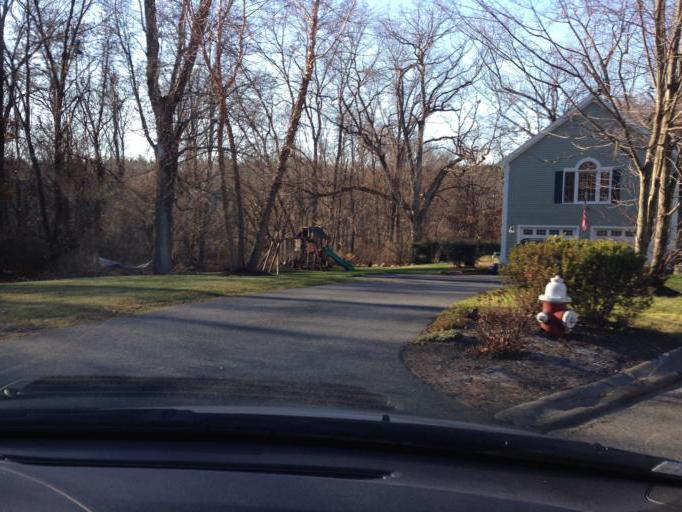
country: US
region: Massachusetts
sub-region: Middlesex County
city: Bedford
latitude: 42.5156
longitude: -71.2721
